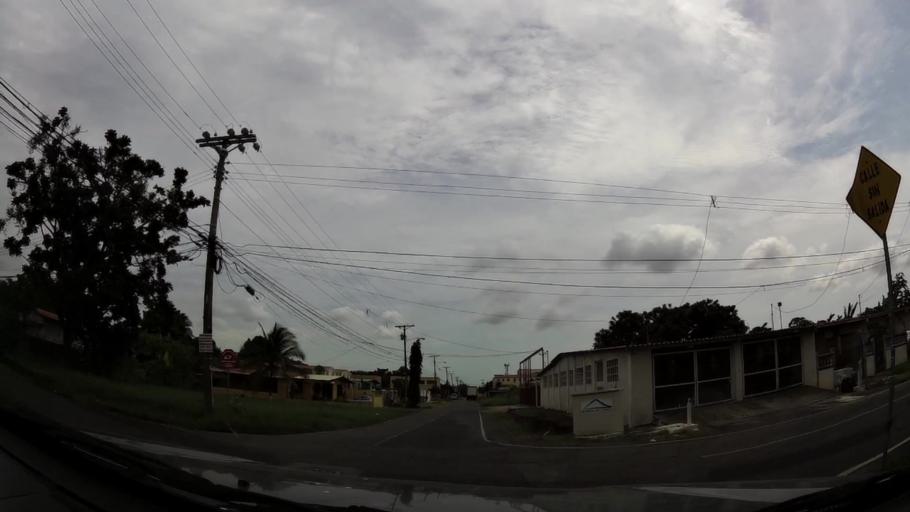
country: PA
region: Panama
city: San Miguelito
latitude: 9.0477
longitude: -79.4249
